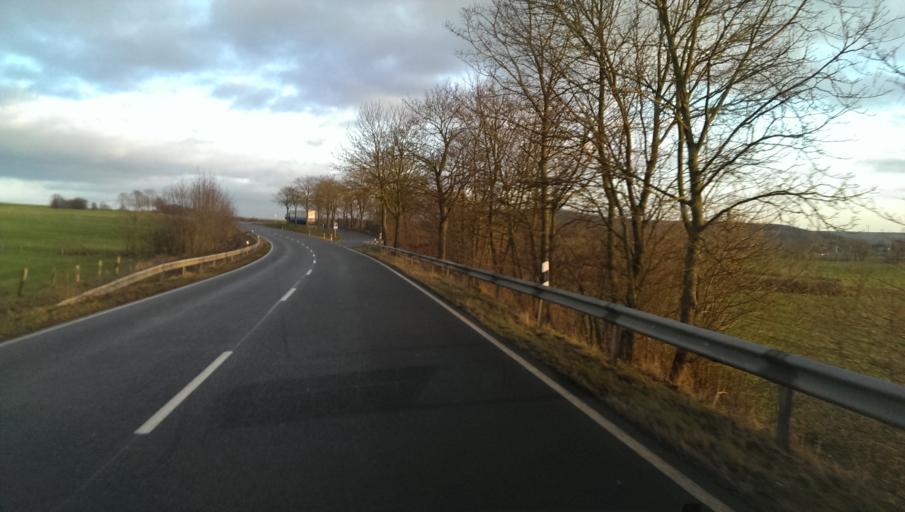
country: DE
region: Lower Saxony
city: Eimen
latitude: 51.8692
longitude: 9.8208
